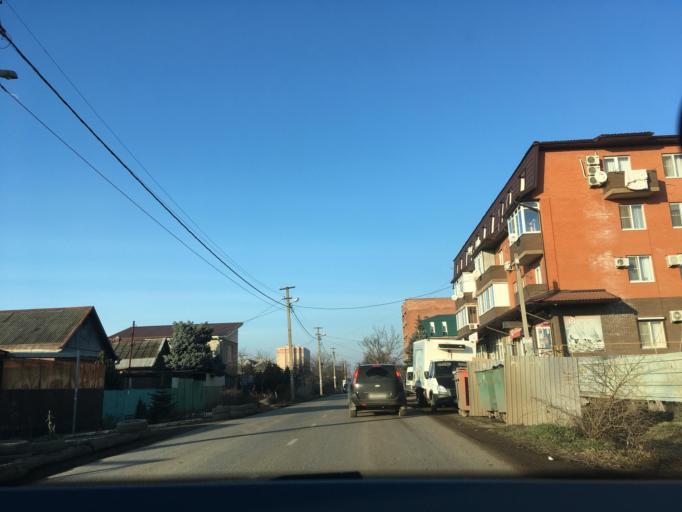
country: RU
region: Krasnodarskiy
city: Krasnodar
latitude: 45.0791
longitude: 39.0207
